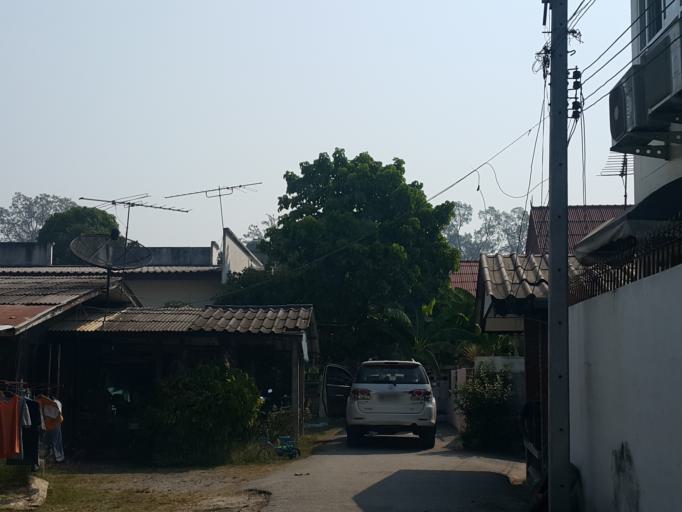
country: TH
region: Chiang Mai
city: Saraphi
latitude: 18.7270
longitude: 99.0218
